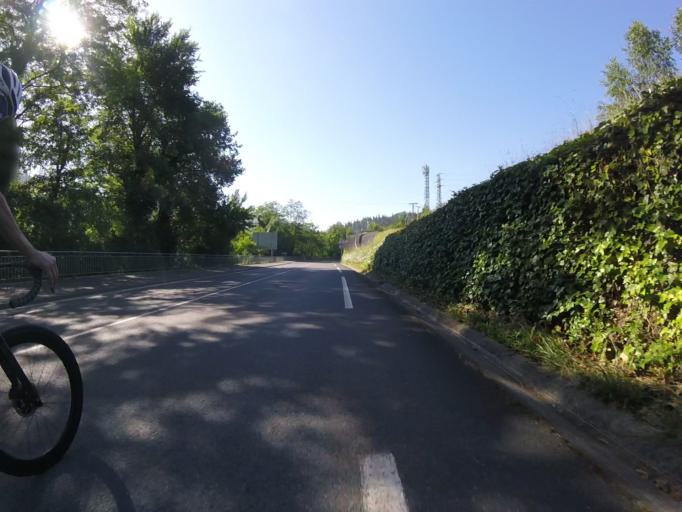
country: ES
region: Basque Country
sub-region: Provincia de Guipuzcoa
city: Azpeitia
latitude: 43.1721
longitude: -2.2559
